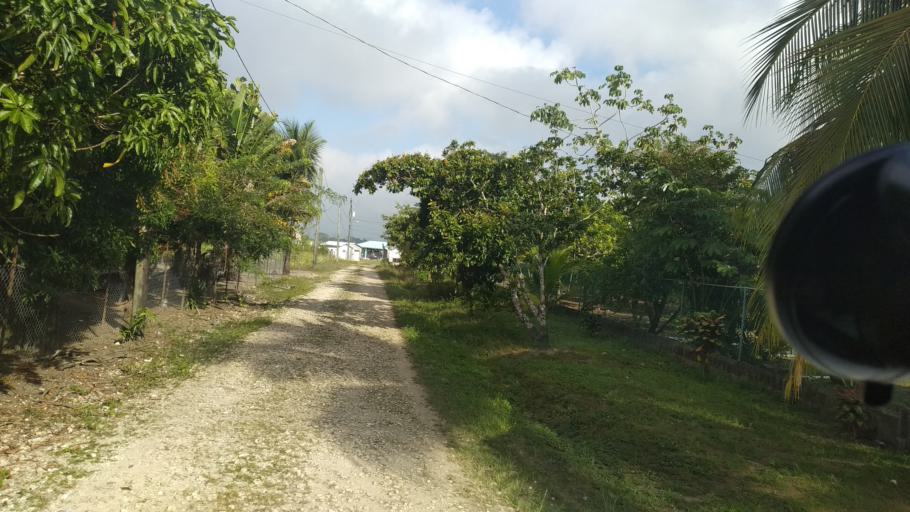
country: BZ
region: Stann Creek
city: Placencia
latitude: 16.5068
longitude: -88.5487
